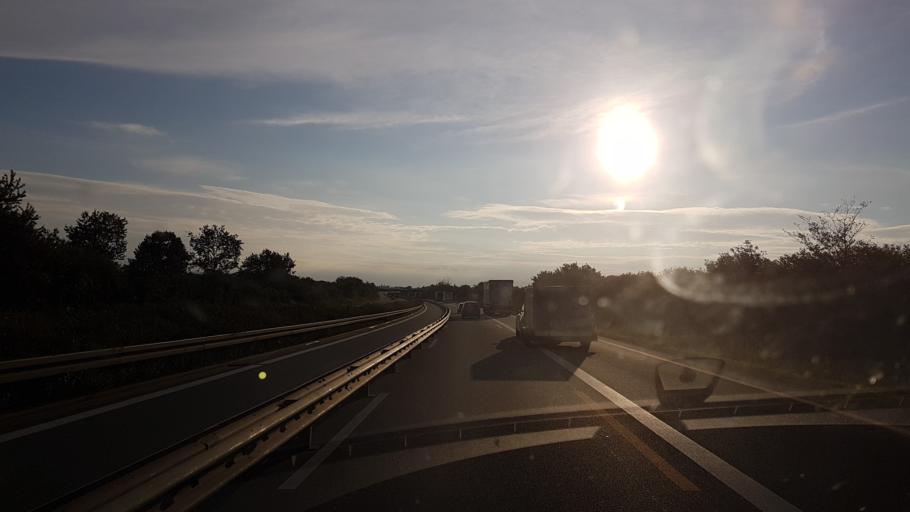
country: DE
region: Saxony
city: Malschwitz
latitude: 51.2059
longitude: 14.4876
